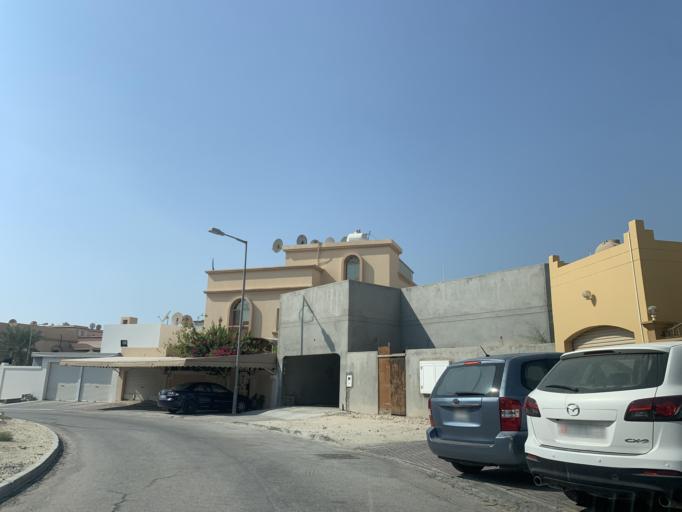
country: BH
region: Central Governorate
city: Madinat Hamad
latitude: 26.1133
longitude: 50.4970
